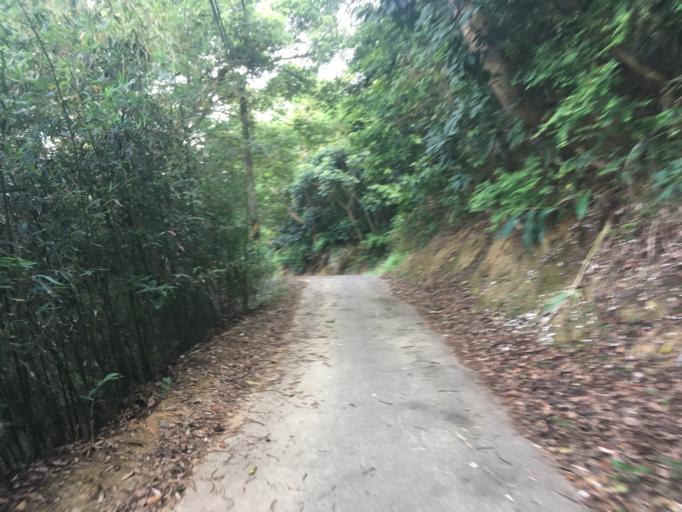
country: TW
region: Taiwan
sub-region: Hsinchu
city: Hsinchu
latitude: 24.7604
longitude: 120.9753
